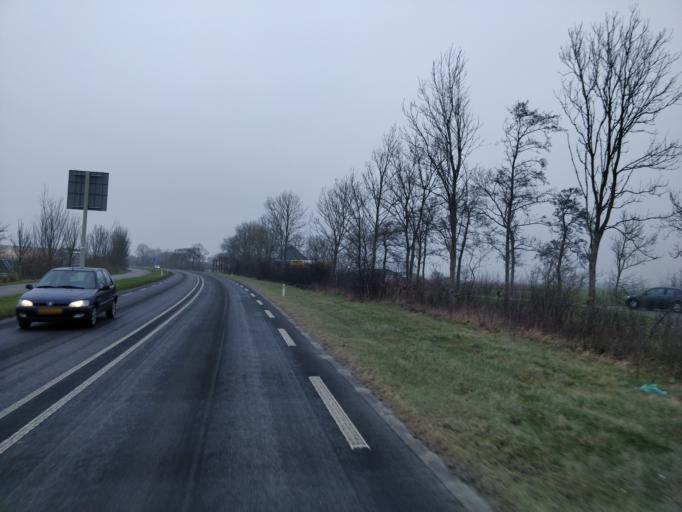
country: NL
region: Friesland
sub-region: Menameradiel
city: Berltsum
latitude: 53.2390
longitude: 5.6762
